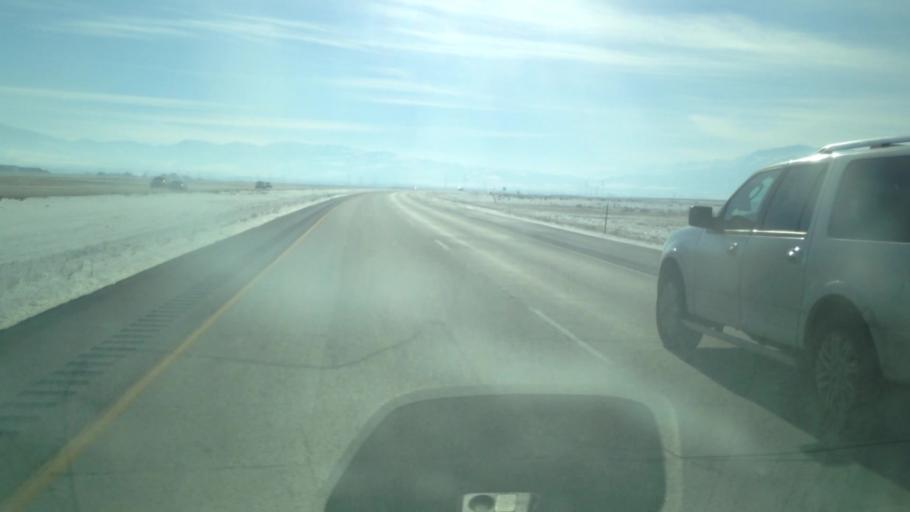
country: US
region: Idaho
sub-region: Oneida County
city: Malad City
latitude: 42.4585
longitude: -112.1700
